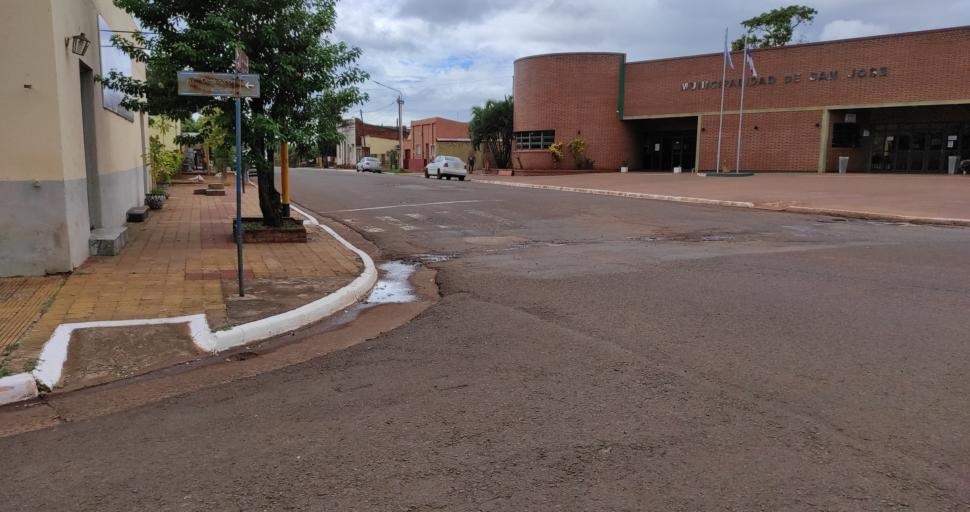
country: AR
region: Misiones
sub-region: Departamento de Apostoles
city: San Jose
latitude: -27.7677
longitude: -55.7774
